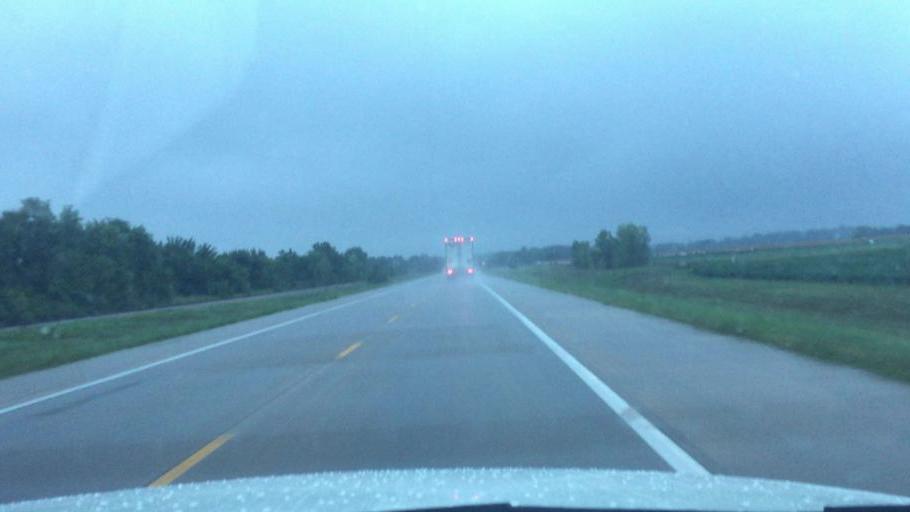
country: US
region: Kansas
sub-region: Neosho County
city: Chanute
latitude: 37.5669
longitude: -95.4712
